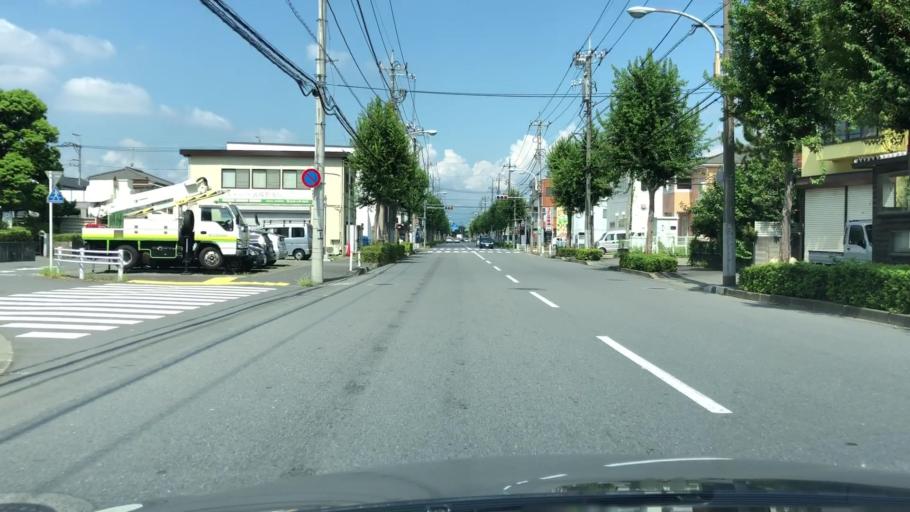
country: JP
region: Tokyo
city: Hino
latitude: 35.6881
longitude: 139.3750
